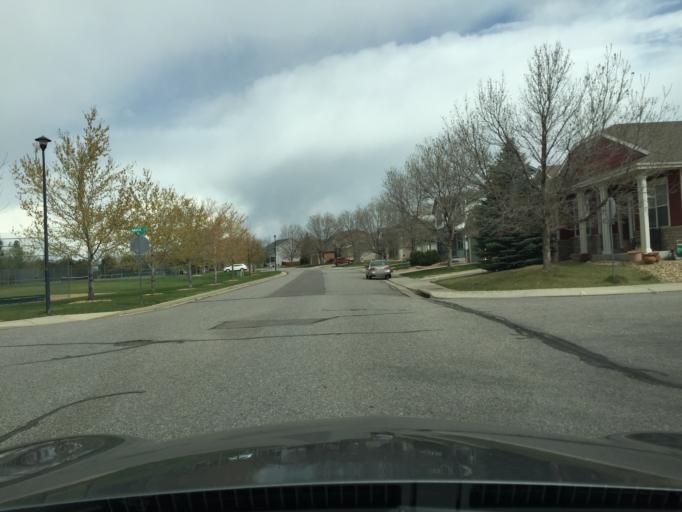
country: US
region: Colorado
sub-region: Boulder County
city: Lafayette
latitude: 40.0169
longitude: -105.0914
